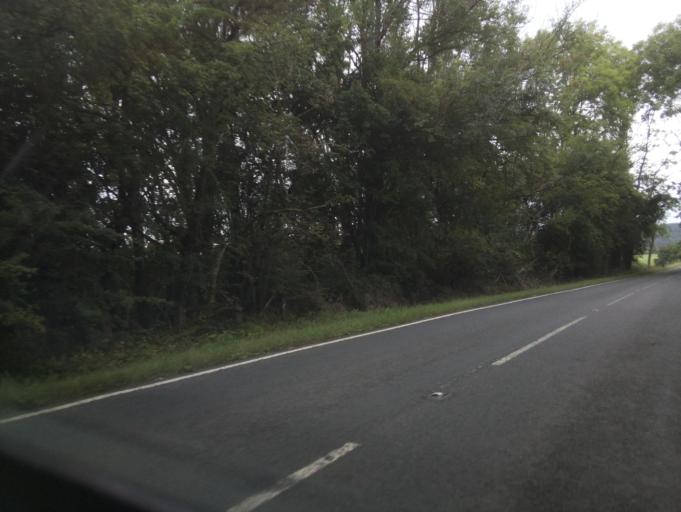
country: GB
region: England
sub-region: North Yorkshire
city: Leyburn
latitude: 54.3925
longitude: -1.8279
